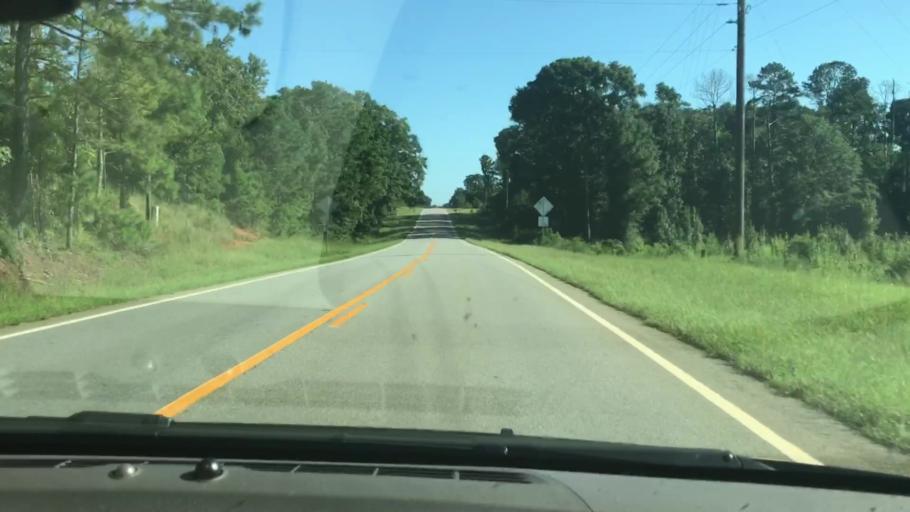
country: US
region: Georgia
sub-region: Quitman County
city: Georgetown
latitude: 31.8485
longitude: -85.0737
